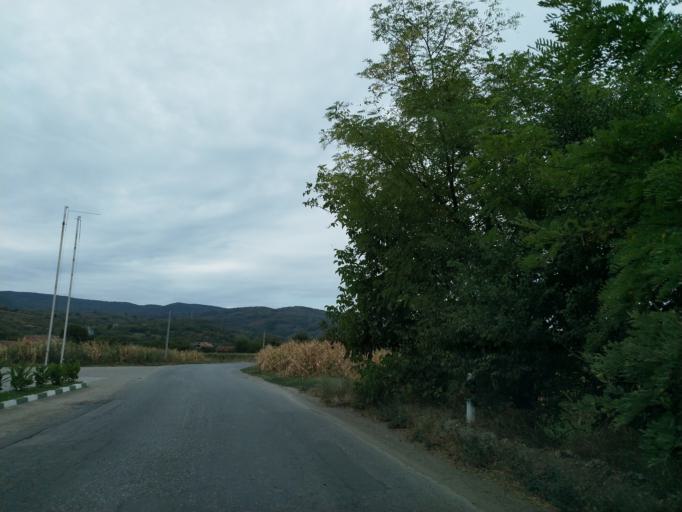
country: RS
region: Central Serbia
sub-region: Pomoravski Okrug
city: Paracin
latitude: 43.8331
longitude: 21.3296
